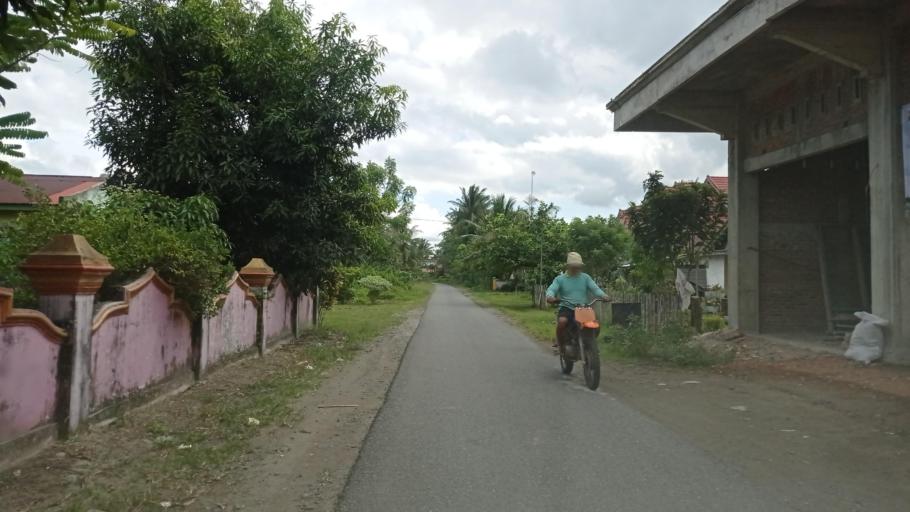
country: ID
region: Jambi
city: Sungai Penuh
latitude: -2.5571
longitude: 101.1027
